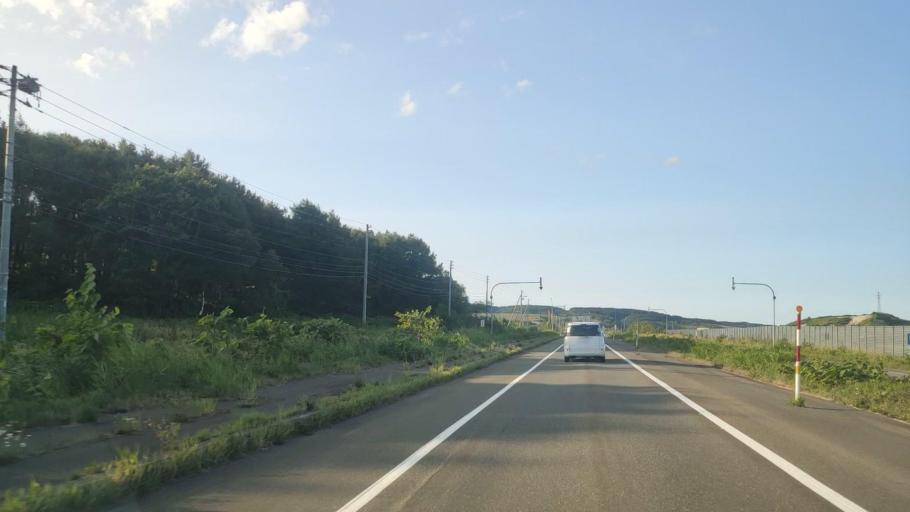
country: JP
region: Hokkaido
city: Wakkanai
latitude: 45.3246
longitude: 141.7196
